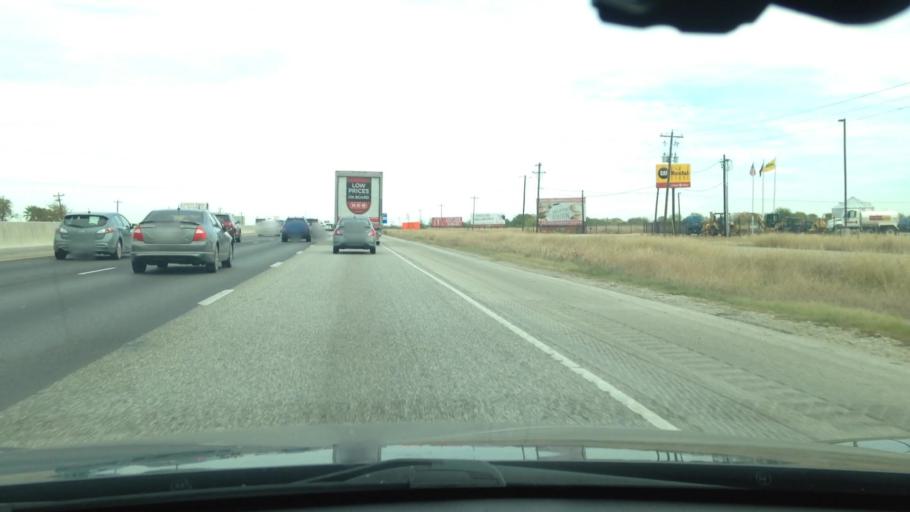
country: US
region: Texas
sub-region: Guadalupe County
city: Redwood
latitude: 29.8012
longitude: -98.0146
